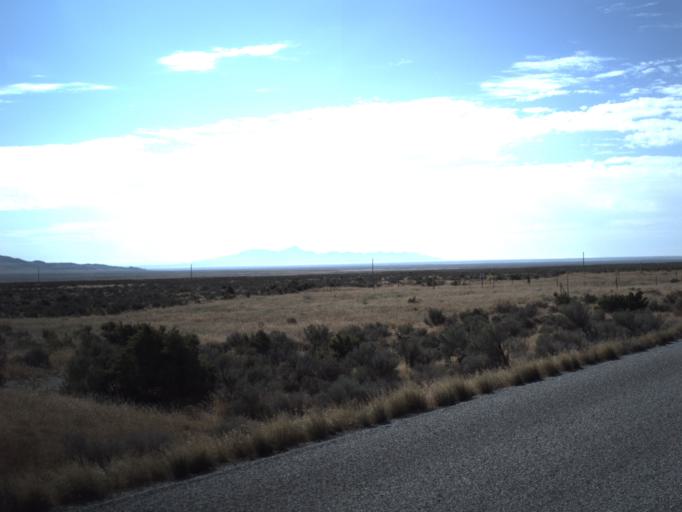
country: US
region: Utah
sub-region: Tooele County
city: Wendover
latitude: 41.5420
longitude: -113.5899
